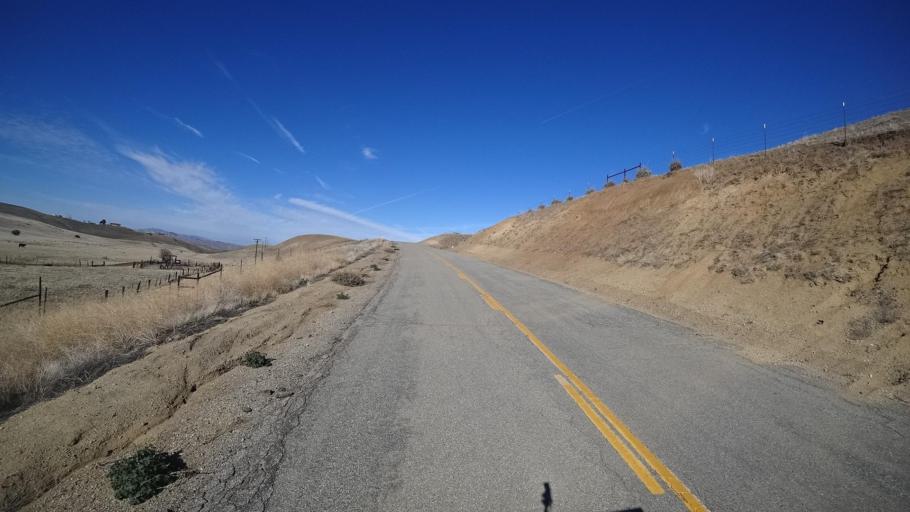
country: US
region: California
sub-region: Kern County
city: Maricopa
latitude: 34.9366
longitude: -119.4021
